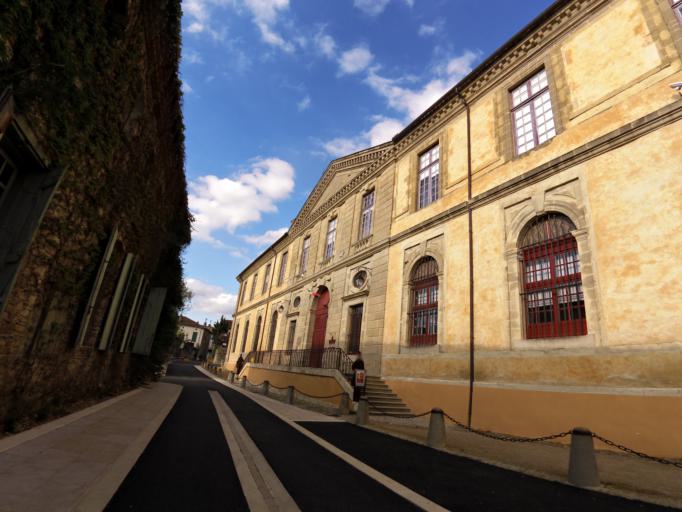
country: FR
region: Midi-Pyrenees
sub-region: Departement du Tarn
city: Soreze
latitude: 43.4515
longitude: 2.0668
